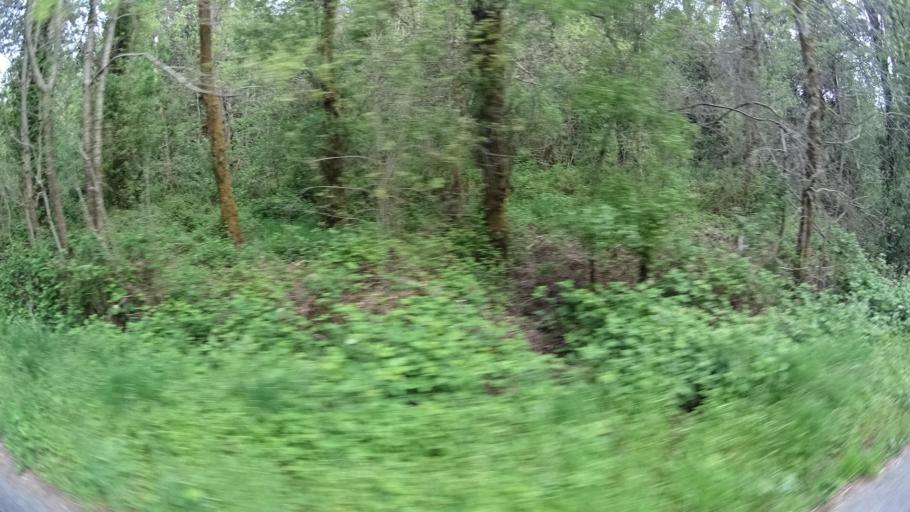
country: US
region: California
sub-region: Humboldt County
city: Redway
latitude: 40.3391
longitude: -123.8978
